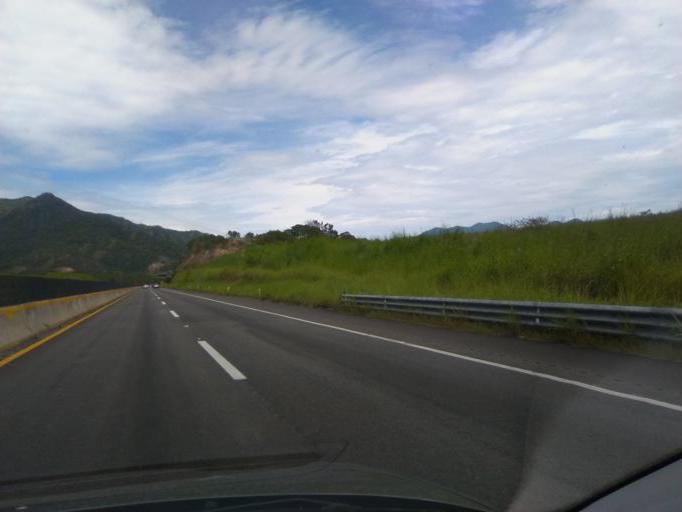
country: MX
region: Guerrero
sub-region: Chilpancingo de los Bravo
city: Cajelitos
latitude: 17.2799
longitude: -99.5078
